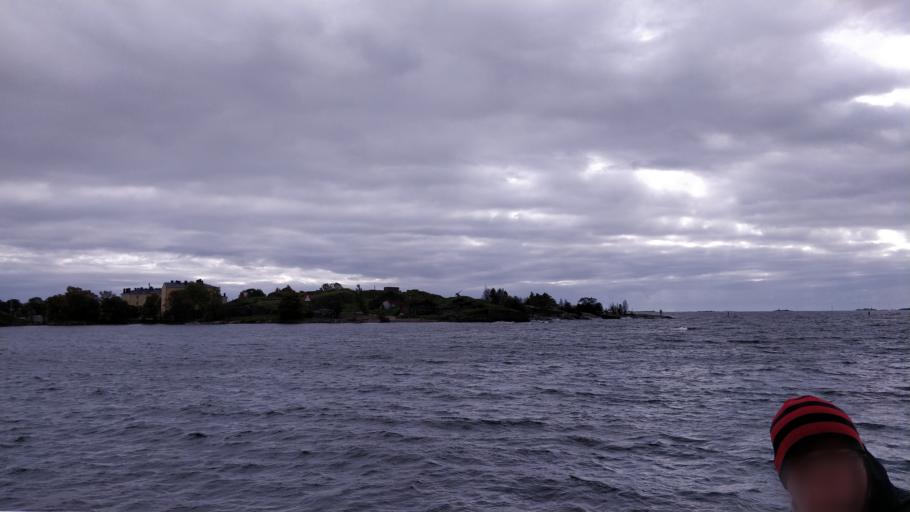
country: FI
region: Uusimaa
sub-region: Helsinki
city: Helsinki
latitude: 60.1515
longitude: 24.9731
